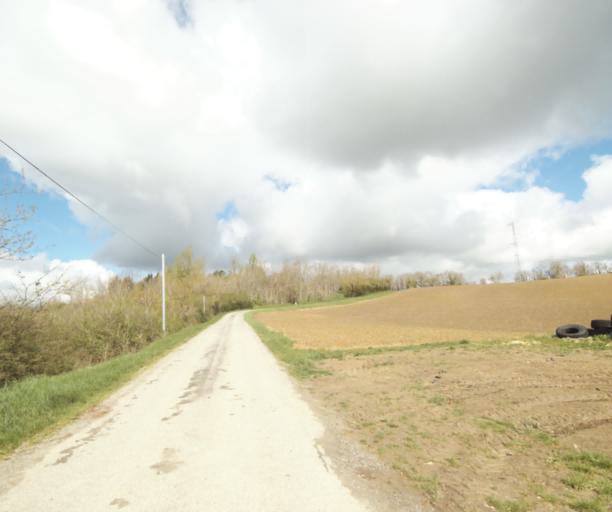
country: FR
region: Midi-Pyrenees
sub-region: Departement de l'Ariege
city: Saverdun
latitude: 43.1898
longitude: 1.5356
